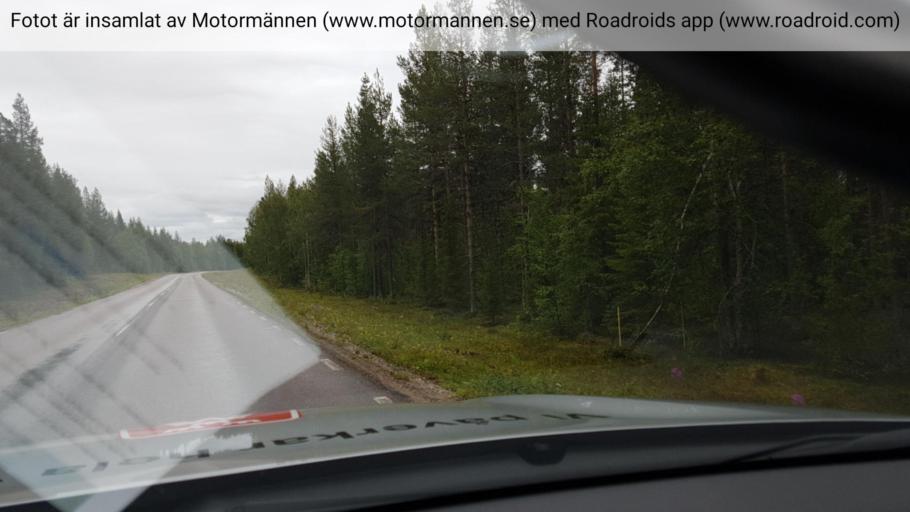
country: SE
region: Norrbotten
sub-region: Overkalix Kommun
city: OEverkalix
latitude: 67.0615
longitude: 22.2838
